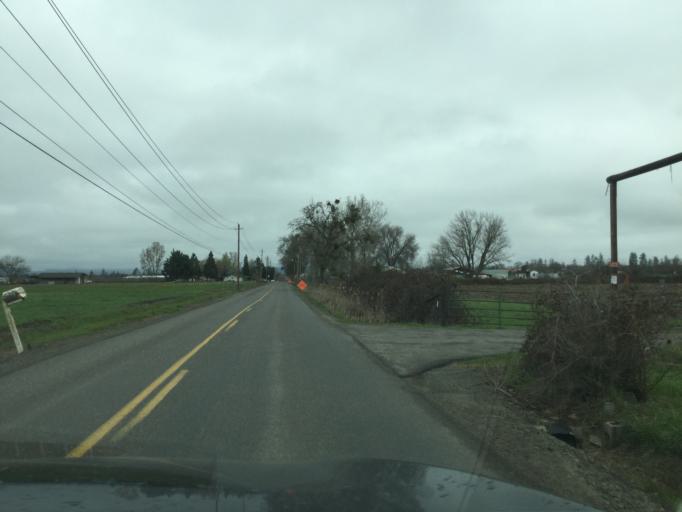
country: US
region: Oregon
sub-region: Jackson County
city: Central Point
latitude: 42.3932
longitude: -122.9093
